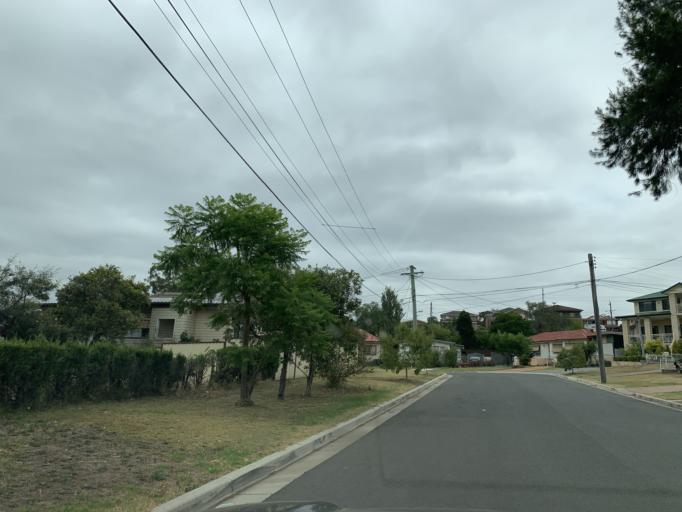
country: AU
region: New South Wales
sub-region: Blacktown
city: Blacktown
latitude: -33.7740
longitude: 150.8937
